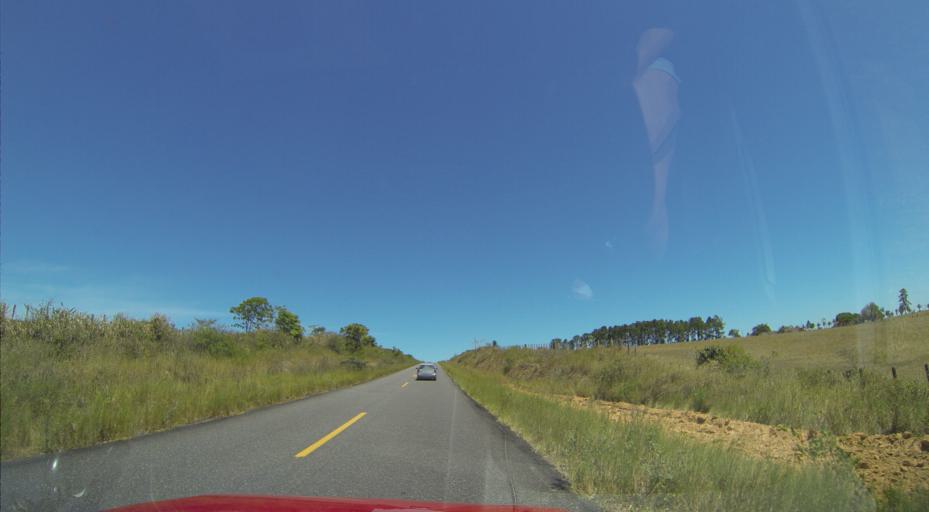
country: BR
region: Bahia
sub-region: Prado
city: Prado
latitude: -17.2308
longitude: -39.3733
